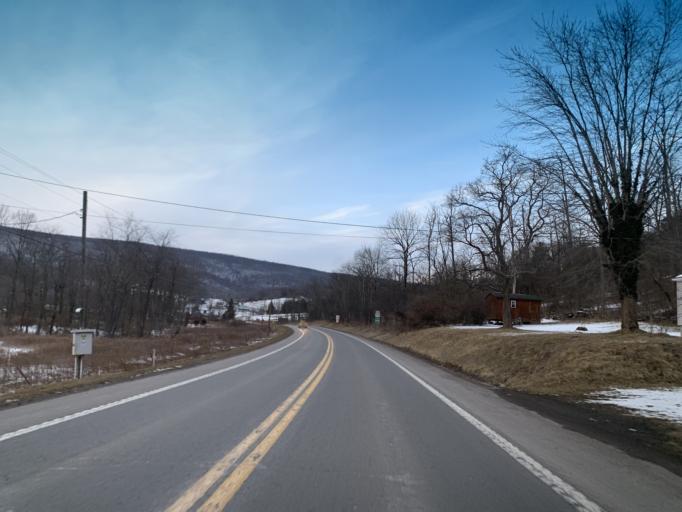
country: US
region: Maryland
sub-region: Allegany County
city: Cumberland
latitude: 39.7239
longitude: -78.7071
